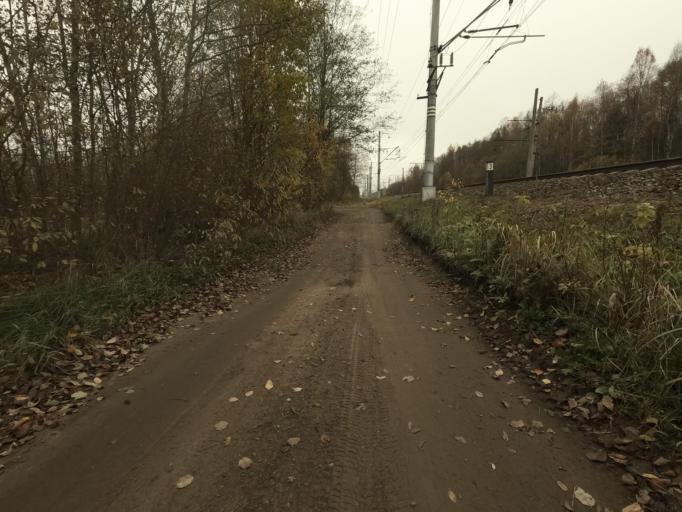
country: RU
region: Leningrad
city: Pavlovo
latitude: 59.7873
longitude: 30.8892
